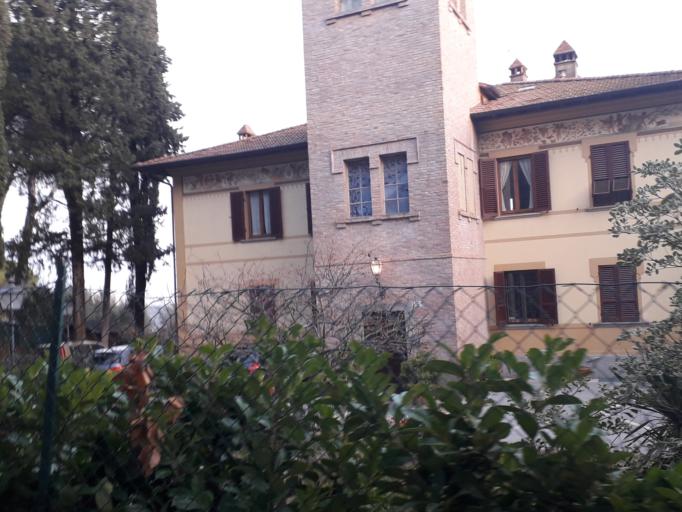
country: IT
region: Umbria
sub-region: Provincia di Perugia
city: Perugia
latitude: 43.0966
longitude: 12.3987
